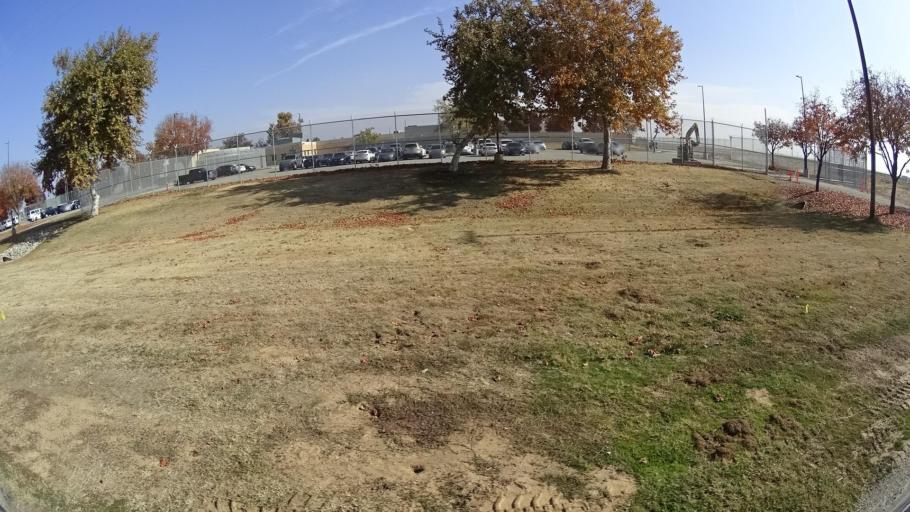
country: US
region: California
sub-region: Kern County
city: Greenacres
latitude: 35.5047
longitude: -119.1167
